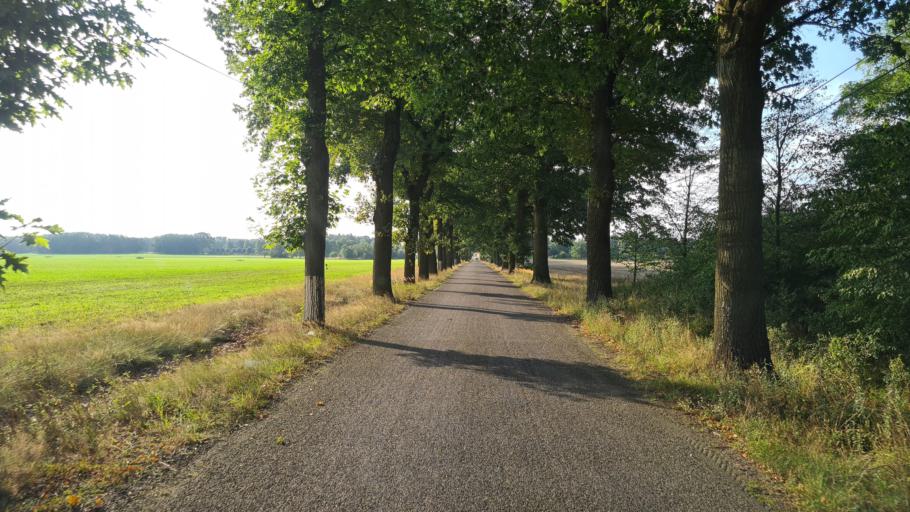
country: DE
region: Brandenburg
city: Neupetershain
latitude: 51.6254
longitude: 14.1026
